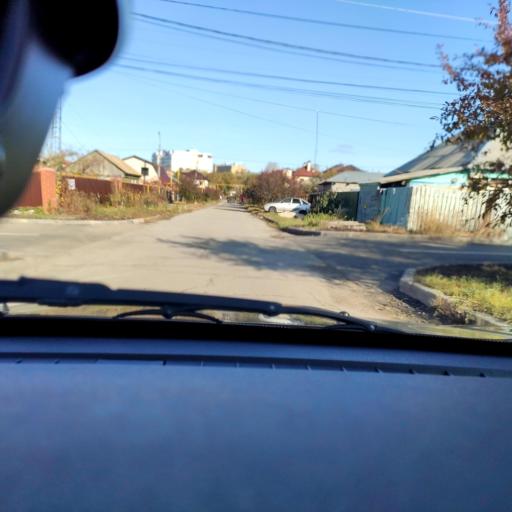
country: RU
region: Samara
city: Tol'yatti
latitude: 53.5279
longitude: 49.4273
